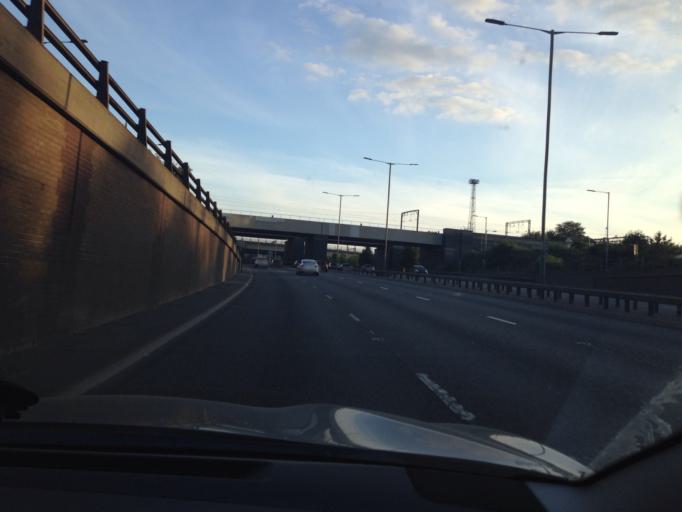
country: GB
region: England
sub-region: Greater London
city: Wembley
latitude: 51.5443
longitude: -0.2732
